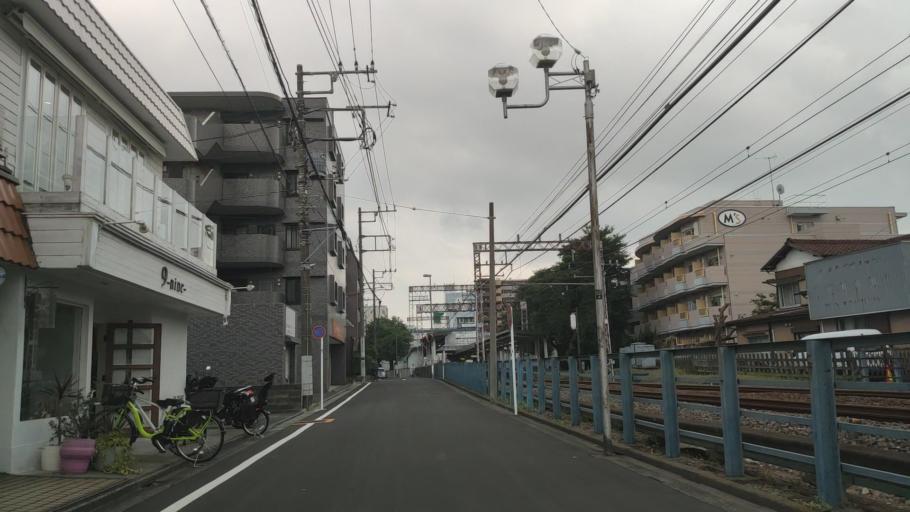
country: JP
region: Kanagawa
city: Minami-rinkan
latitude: 35.4917
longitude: 139.4502
